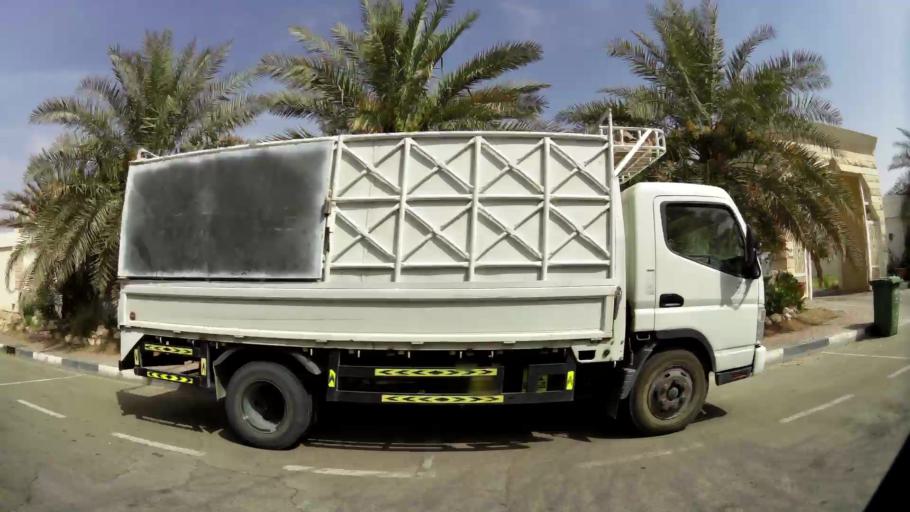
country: AE
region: Abu Dhabi
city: Al Ain
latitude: 24.1608
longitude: 55.6947
